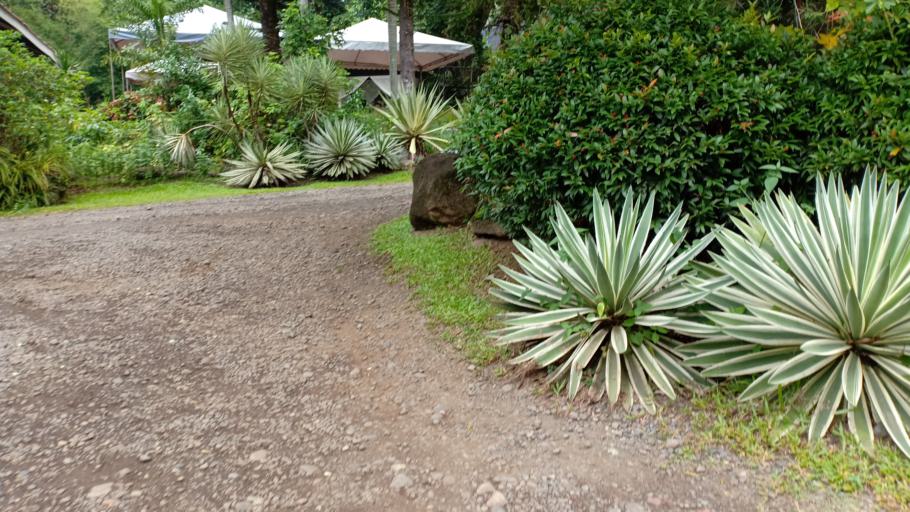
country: PH
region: Davao
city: Malagos
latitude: 7.1905
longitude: 125.4281
